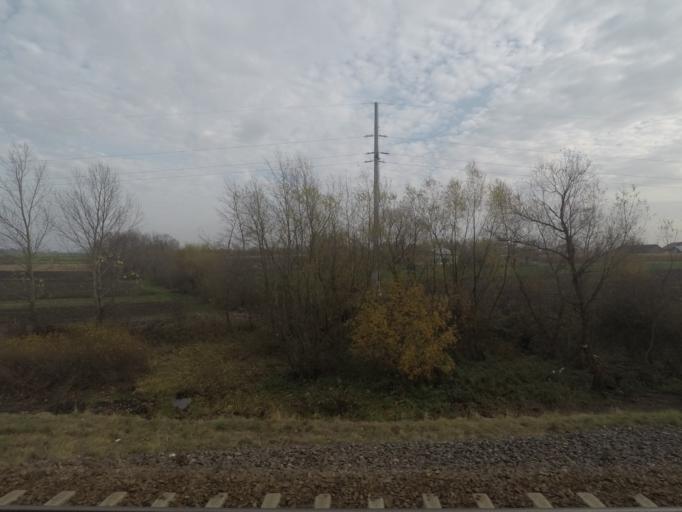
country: PL
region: Subcarpathian Voivodeship
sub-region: Powiat jaroslawski
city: Sosnica
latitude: 49.8658
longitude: 22.8589
